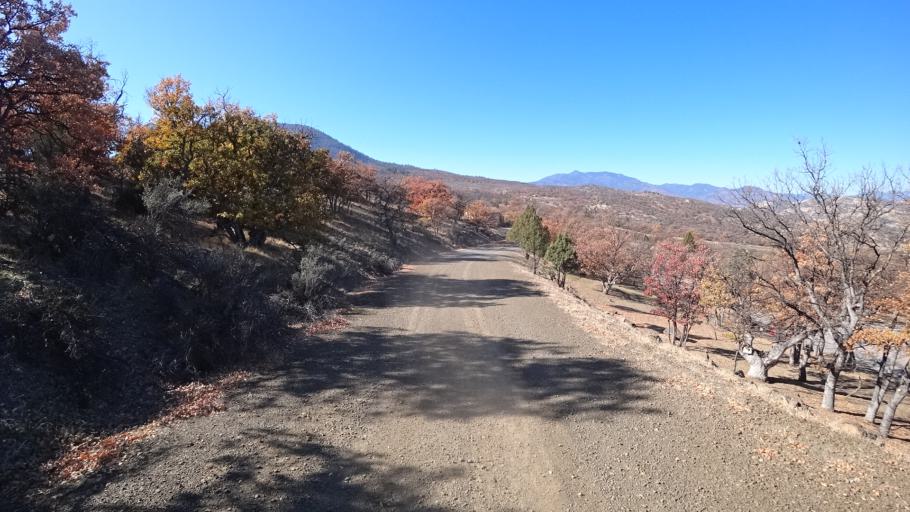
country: US
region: California
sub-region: Siskiyou County
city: Montague
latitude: 41.8840
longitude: -122.4830
